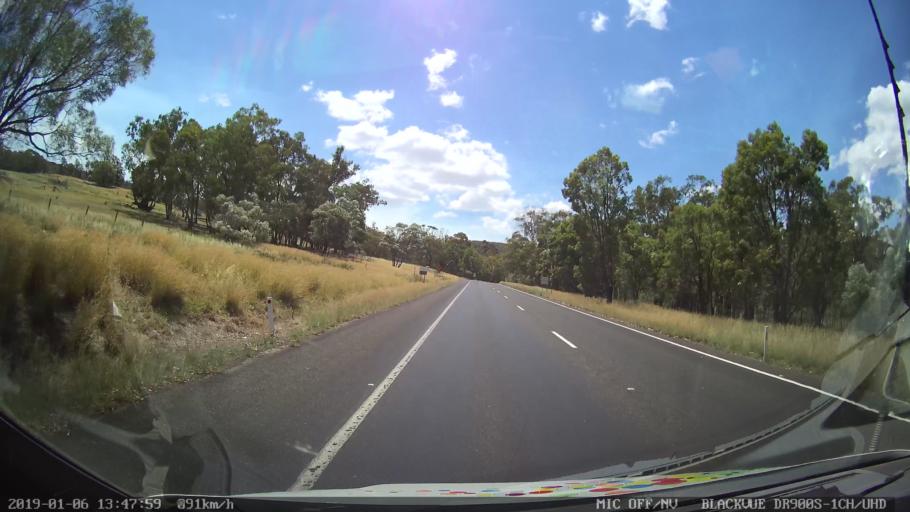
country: AU
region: New South Wales
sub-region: Tamworth Municipality
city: Kootingal
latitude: -30.9572
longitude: 151.1064
